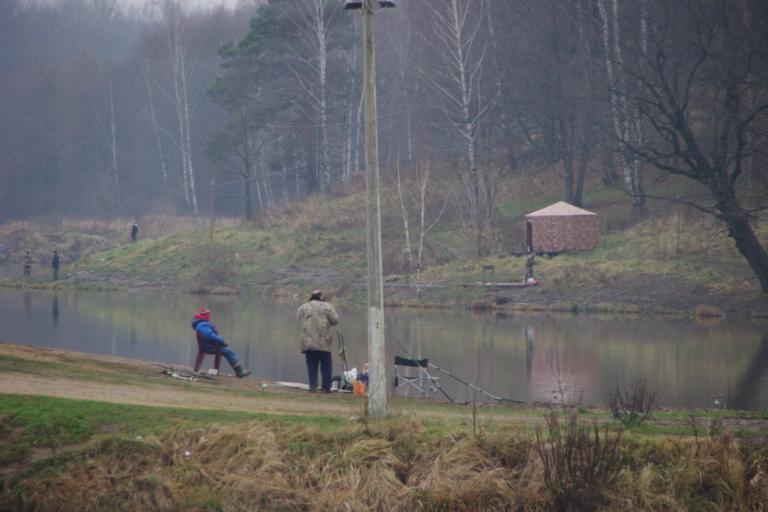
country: RU
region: Moskovskaya
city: Krasnogorsk
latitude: 55.8398
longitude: 37.3259
